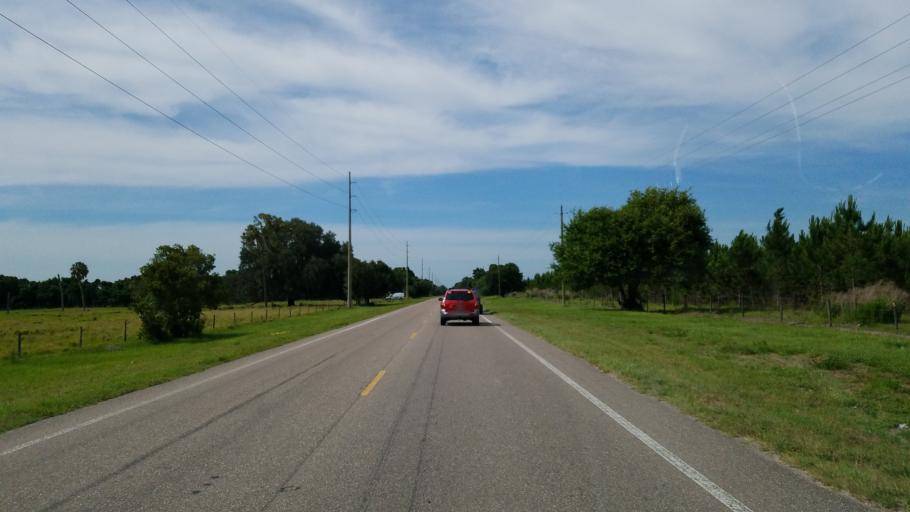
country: US
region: Florida
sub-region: Hillsborough County
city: Balm
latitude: 27.6724
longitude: -82.1462
